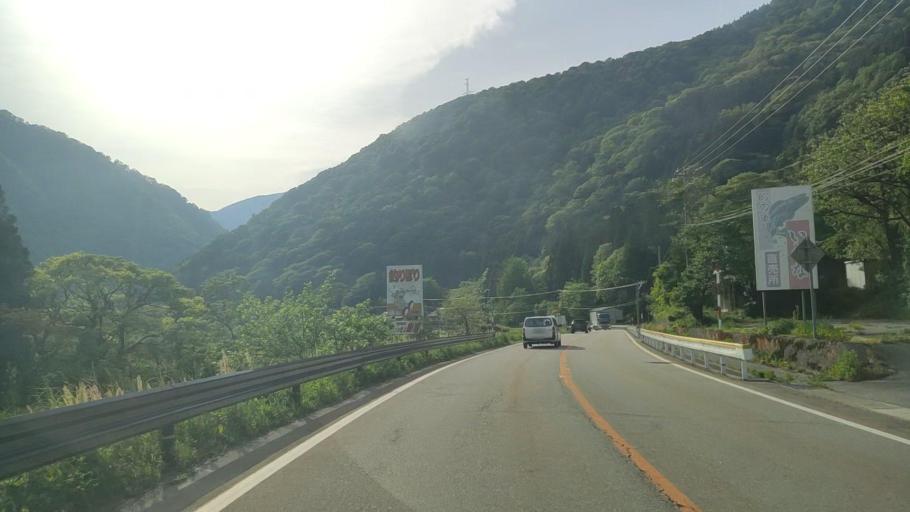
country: JP
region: Toyama
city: Yatsuomachi-higashikumisaka
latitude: 36.4496
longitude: 137.2696
